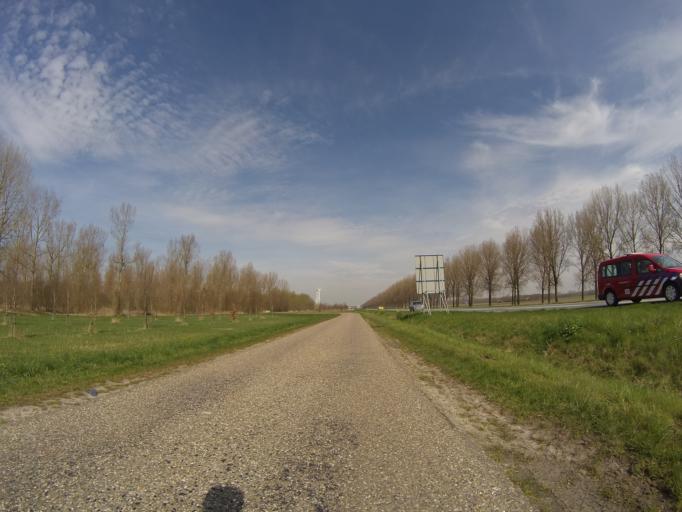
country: NL
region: Gelderland
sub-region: Gemeente Nijkerk
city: Nijkerk
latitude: 52.2697
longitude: 5.4674
